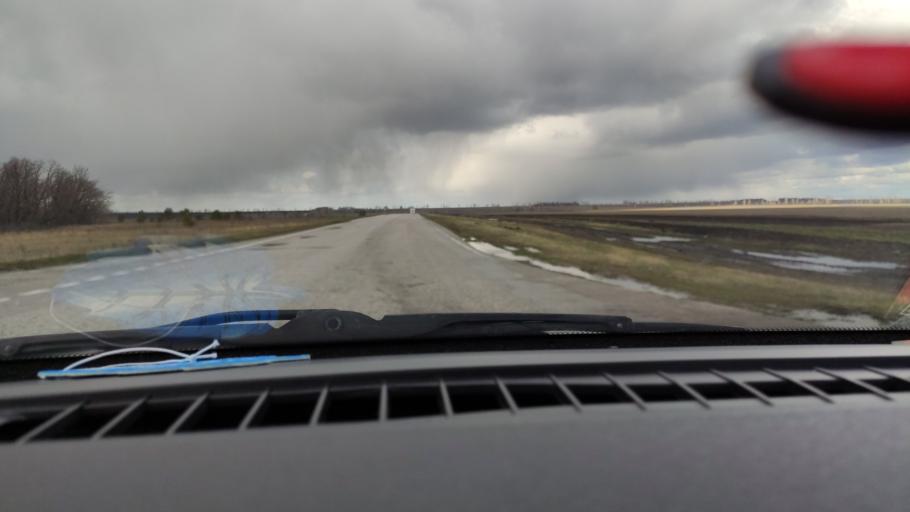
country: RU
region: Samara
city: Povolzhskiy
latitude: 53.7937
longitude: 49.7353
